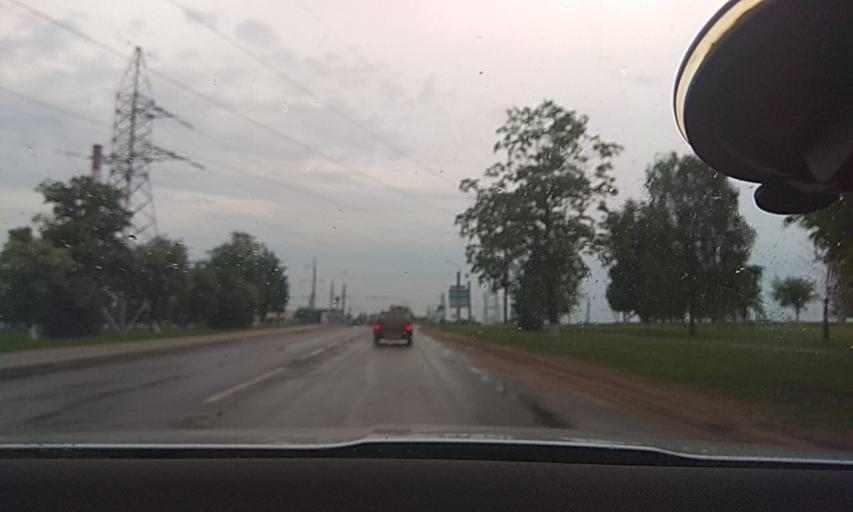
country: BY
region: Grodnenskaya
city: Hrodna
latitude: 53.6739
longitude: 23.8898
